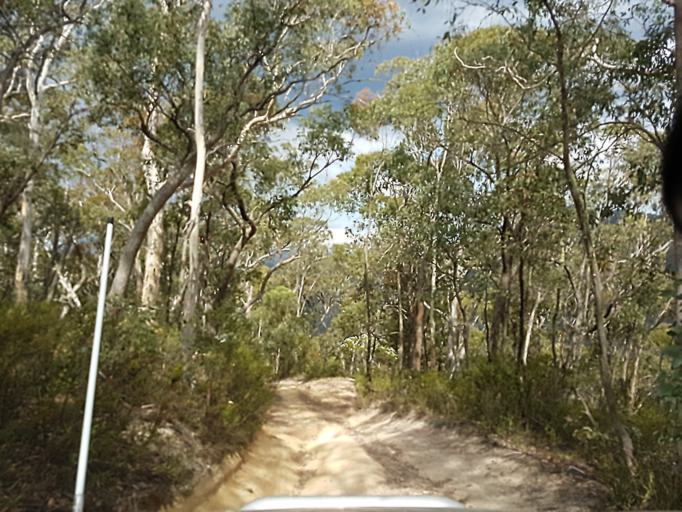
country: AU
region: New South Wales
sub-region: Snowy River
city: Jindabyne
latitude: -36.8806
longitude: 148.2136
